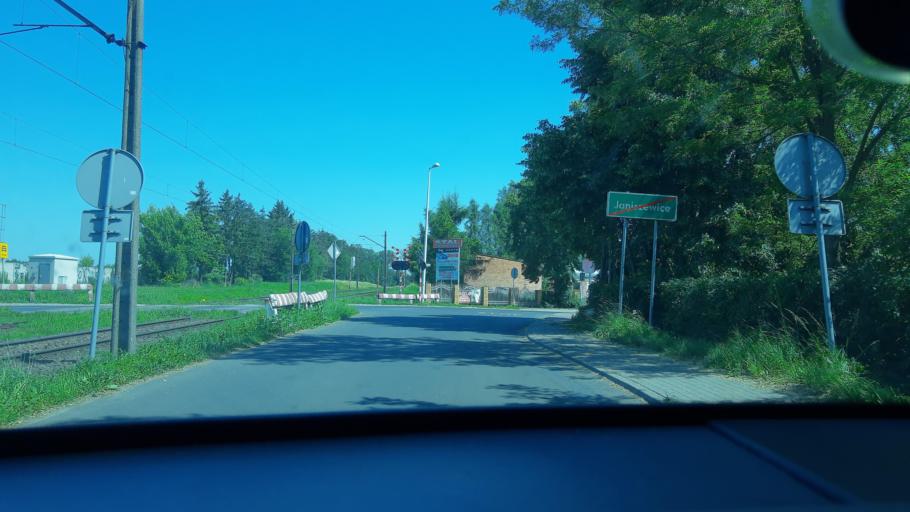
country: PL
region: Lodz Voivodeship
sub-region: Powiat zdunskowolski
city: Zdunska Wola
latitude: 51.6210
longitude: 18.9647
